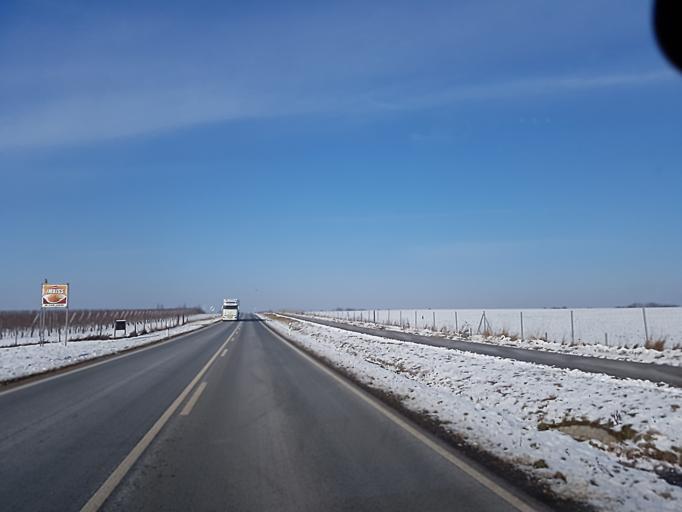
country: DE
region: Saxony
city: Leisnig
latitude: 51.1435
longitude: 12.9425
